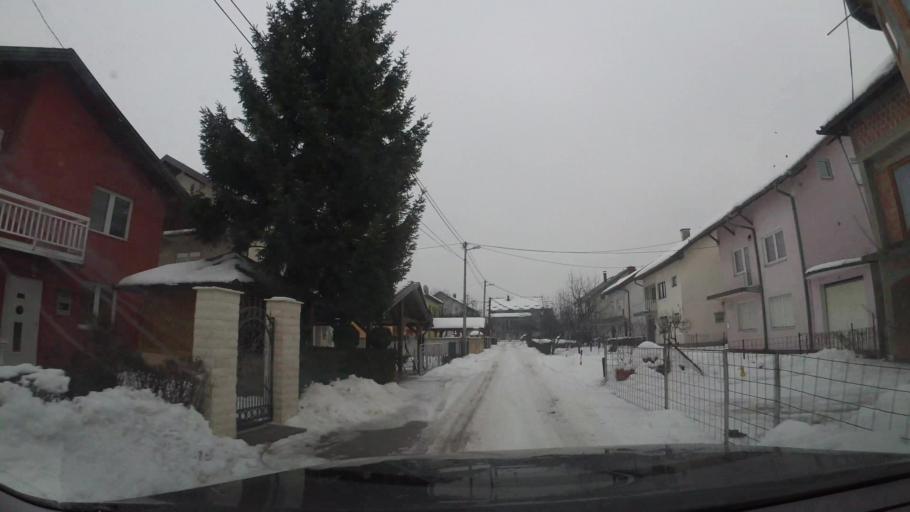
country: BA
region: Federation of Bosnia and Herzegovina
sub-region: Kanton Sarajevo
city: Sarajevo
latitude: 43.8403
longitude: 18.3011
